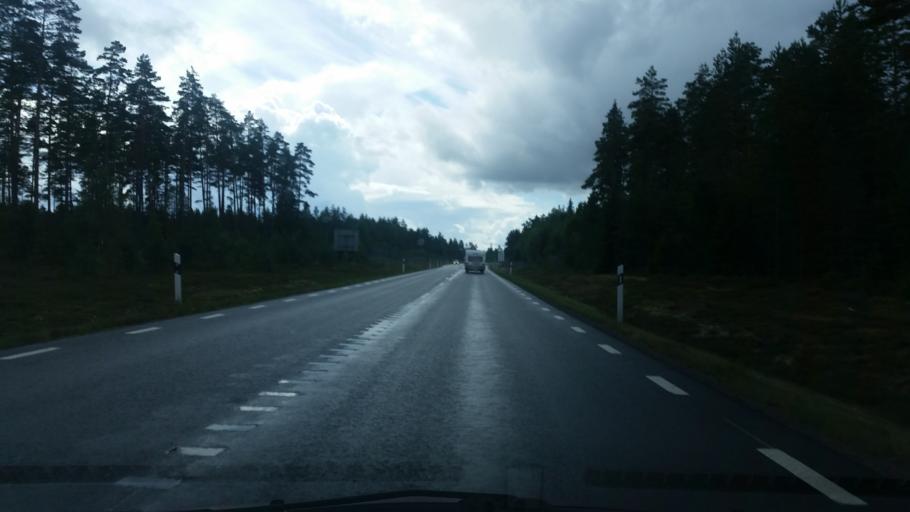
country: SE
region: Joenkoeping
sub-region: Gislaveds Kommun
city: Gislaved
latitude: 57.3531
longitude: 13.5577
